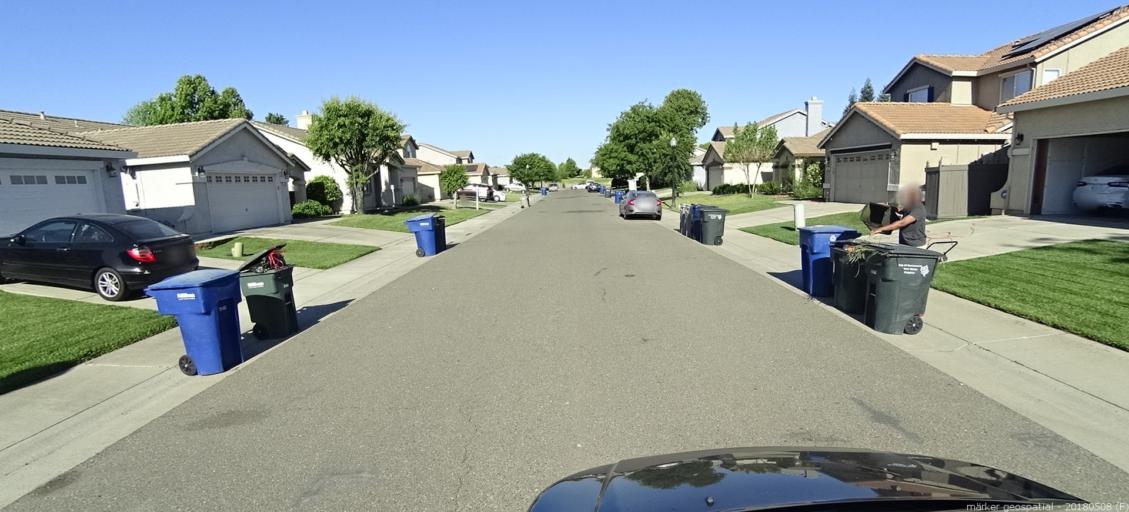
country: US
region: California
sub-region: Sacramento County
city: Elverta
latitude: 38.6767
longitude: -121.5055
